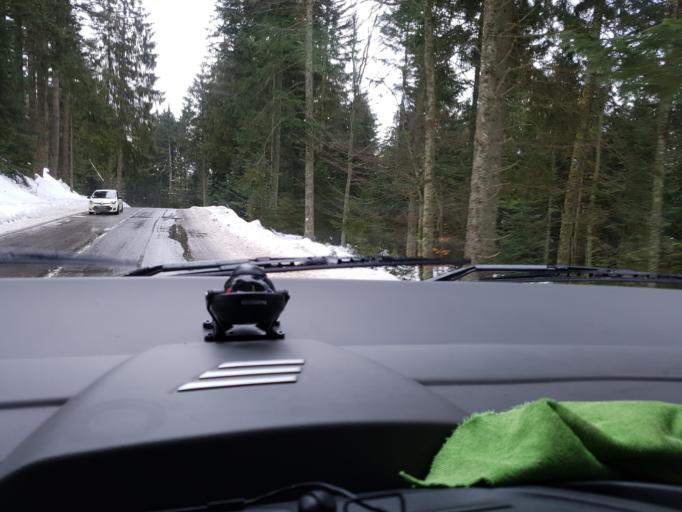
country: FR
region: Lorraine
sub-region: Departement des Vosges
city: Plainfaing
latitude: 48.1453
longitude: 7.0674
